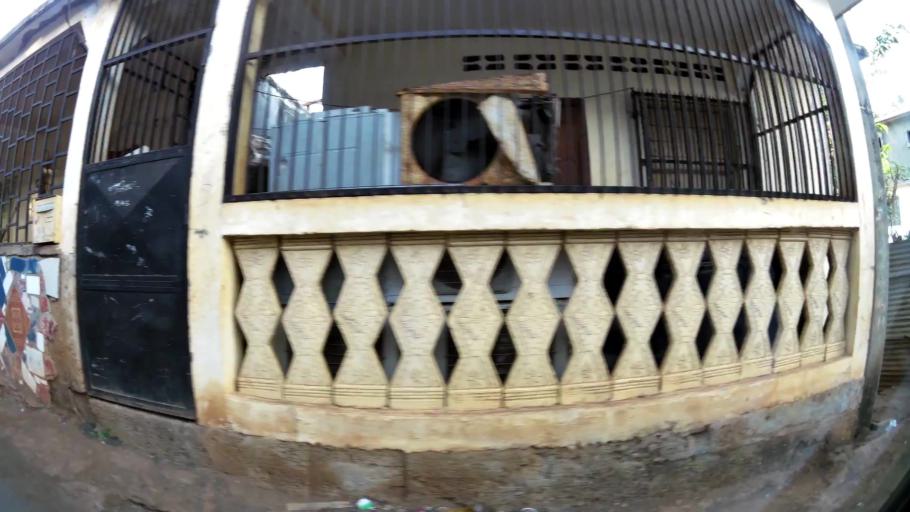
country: YT
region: Dembeni
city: Dembeni
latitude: -12.8371
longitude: 45.1738
